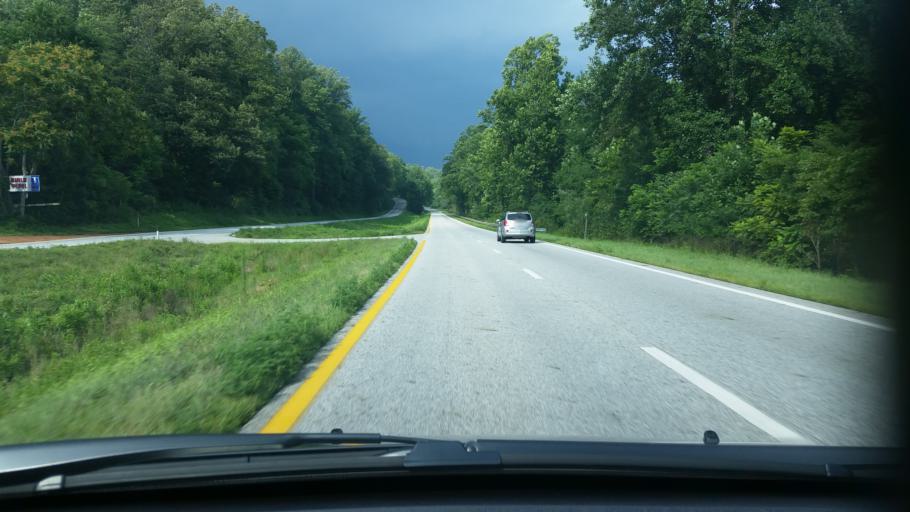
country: US
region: Virginia
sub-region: Nelson County
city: Lovingston
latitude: 37.8198
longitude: -78.8444
